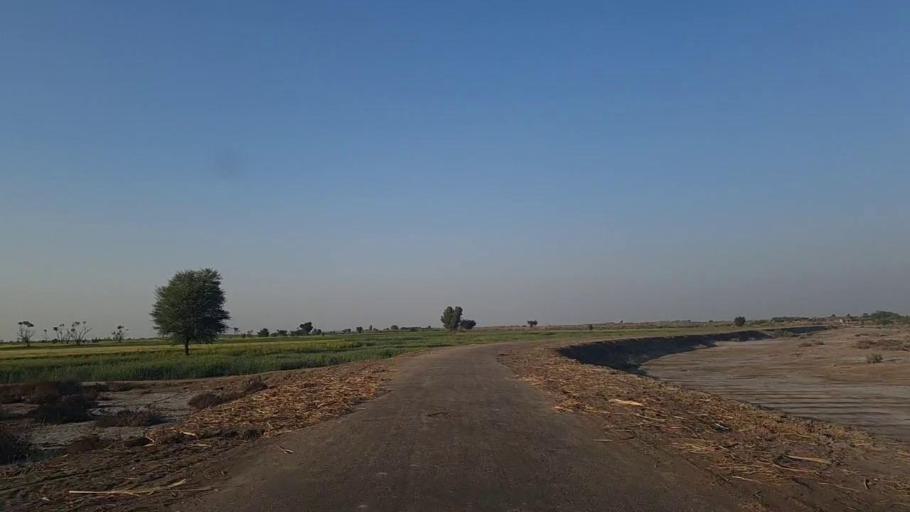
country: PK
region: Sindh
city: Jam Sahib
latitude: 26.3365
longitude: 68.6677
